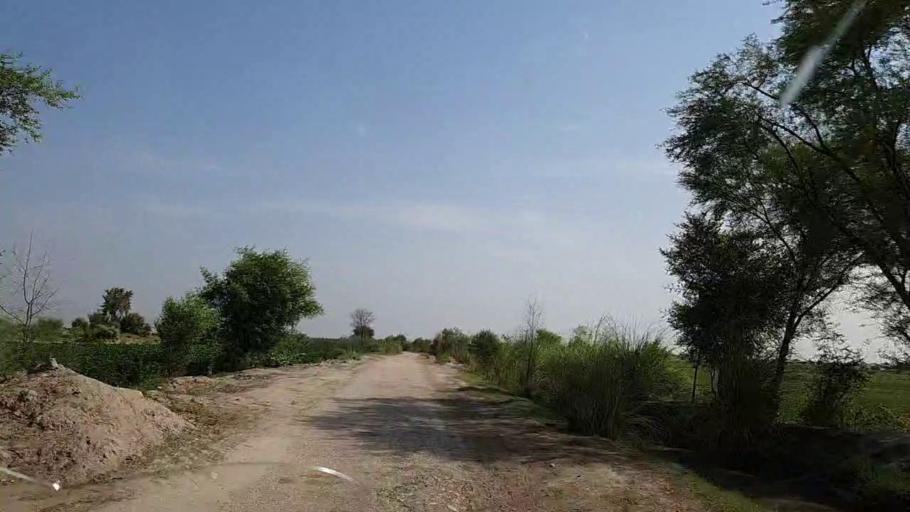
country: PK
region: Sindh
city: Khanpur
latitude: 27.7204
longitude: 69.3608
